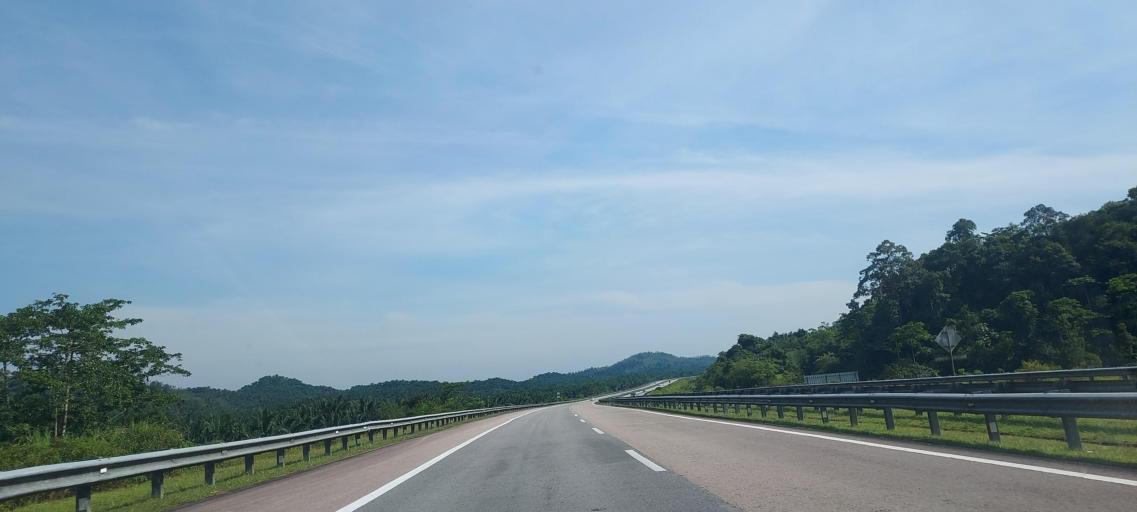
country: MY
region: Terengganu
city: Marang
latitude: 4.9544
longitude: 103.0848
